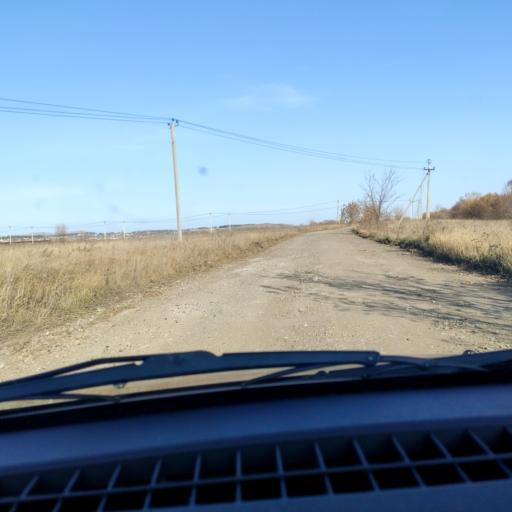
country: RU
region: Bashkortostan
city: Avdon
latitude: 54.4958
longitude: 55.8633
